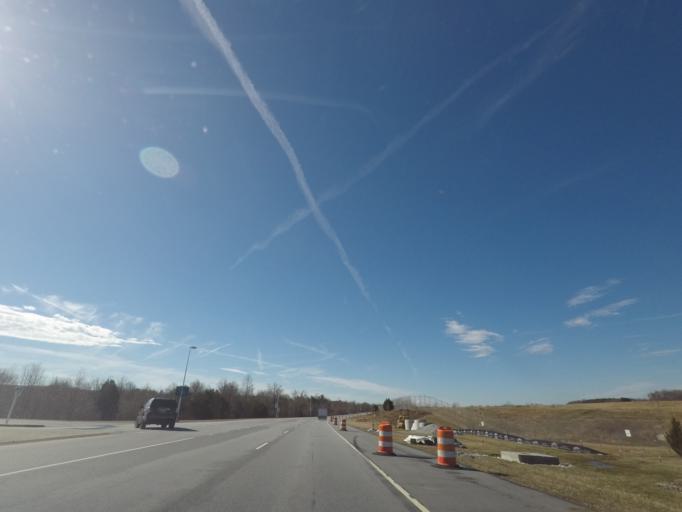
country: US
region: North Carolina
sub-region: Guilford County
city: Oak Ridge
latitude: 36.1129
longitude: -79.9370
